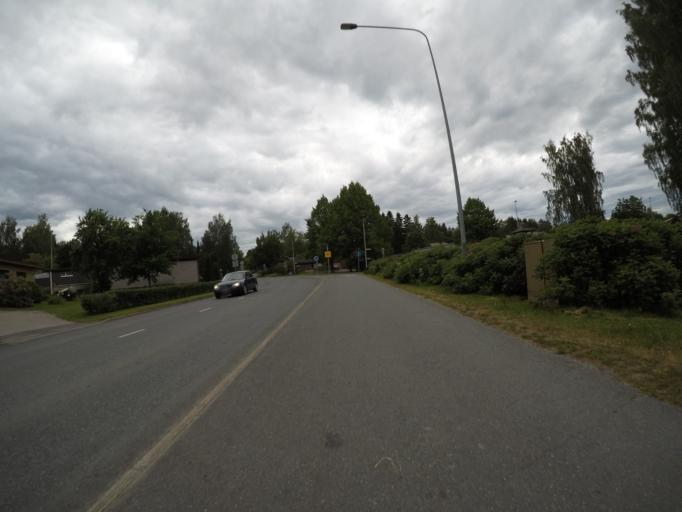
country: FI
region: Haeme
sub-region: Haemeenlinna
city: Haemeenlinna
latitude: 60.9781
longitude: 24.4640
